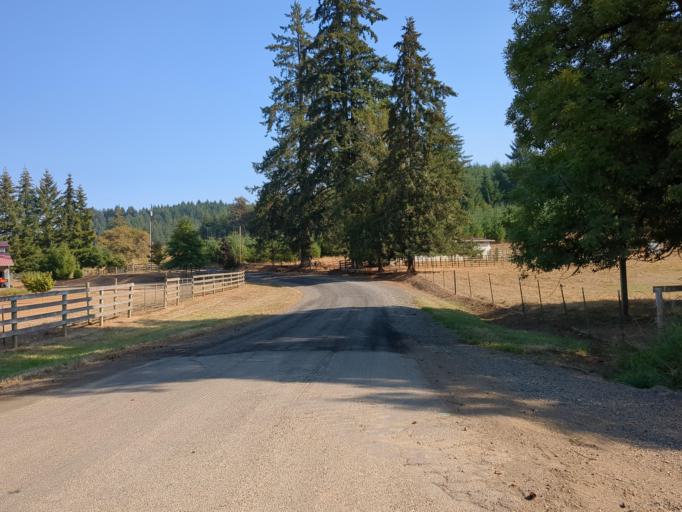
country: US
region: Oregon
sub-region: Lane County
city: Junction City
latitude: 44.2942
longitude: -123.3586
